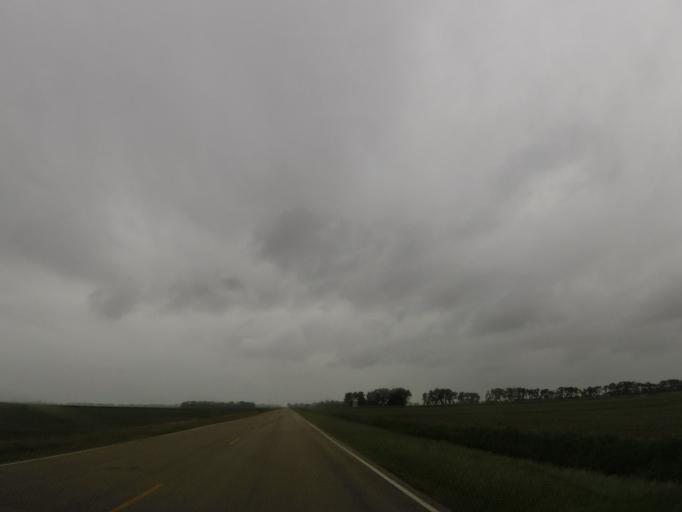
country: US
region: North Dakota
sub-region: Walsh County
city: Grafton
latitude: 48.5607
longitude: -97.2999
